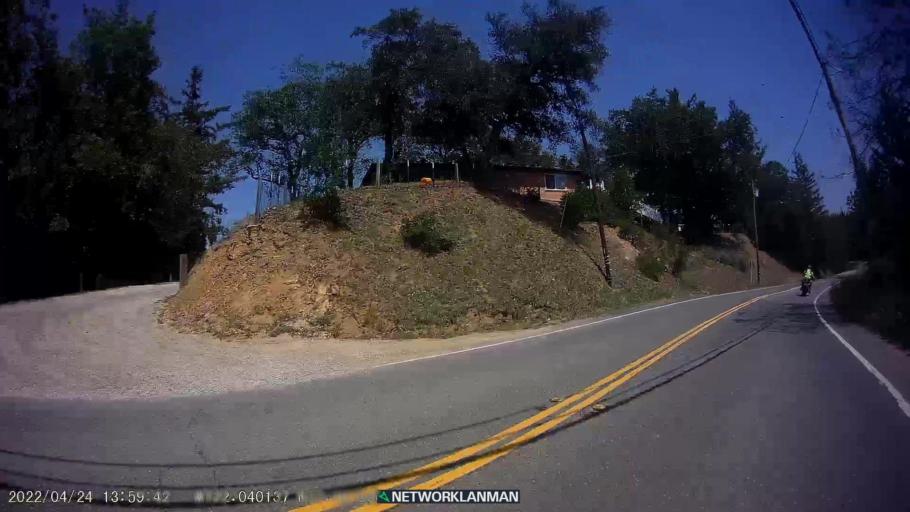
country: US
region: California
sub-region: Santa Cruz County
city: Lompico
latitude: 37.1679
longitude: -122.0397
